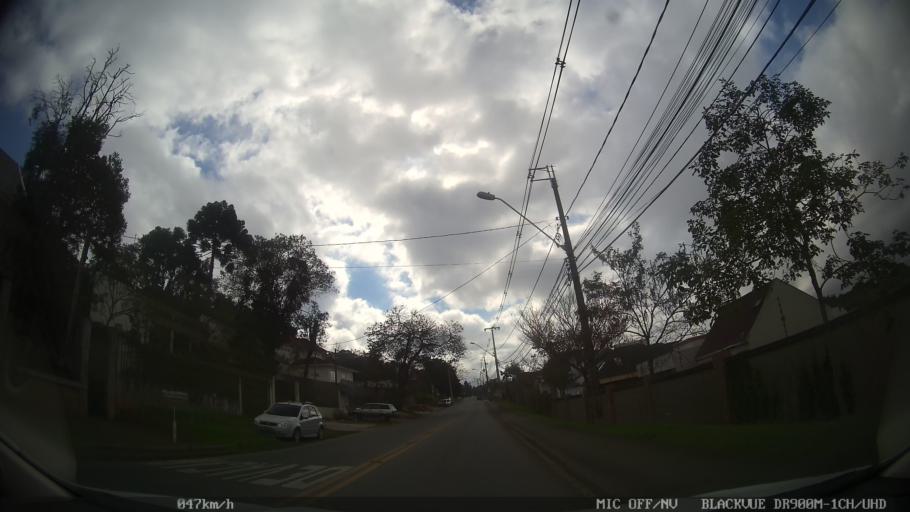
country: BR
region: Parana
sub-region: Curitiba
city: Curitiba
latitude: -25.3643
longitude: -49.2500
